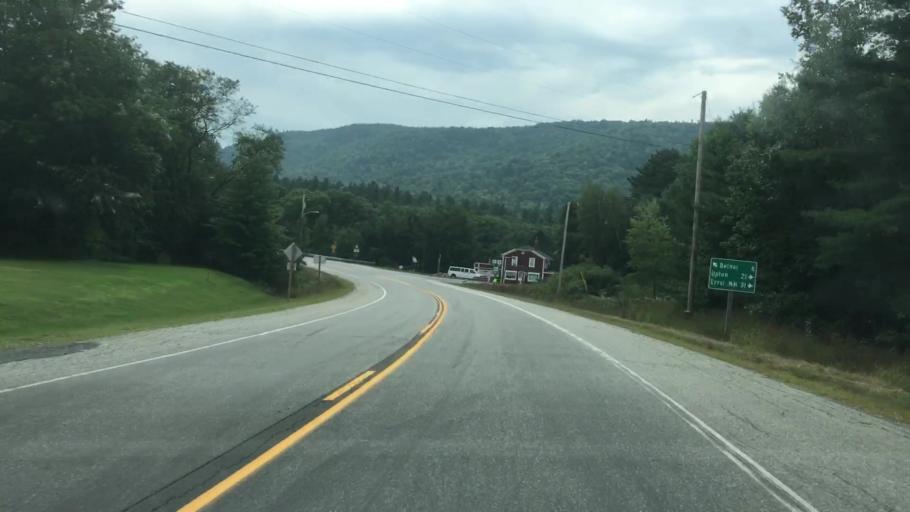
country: US
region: Maine
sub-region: Oxford County
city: Bethel
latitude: 44.4878
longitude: -70.7859
